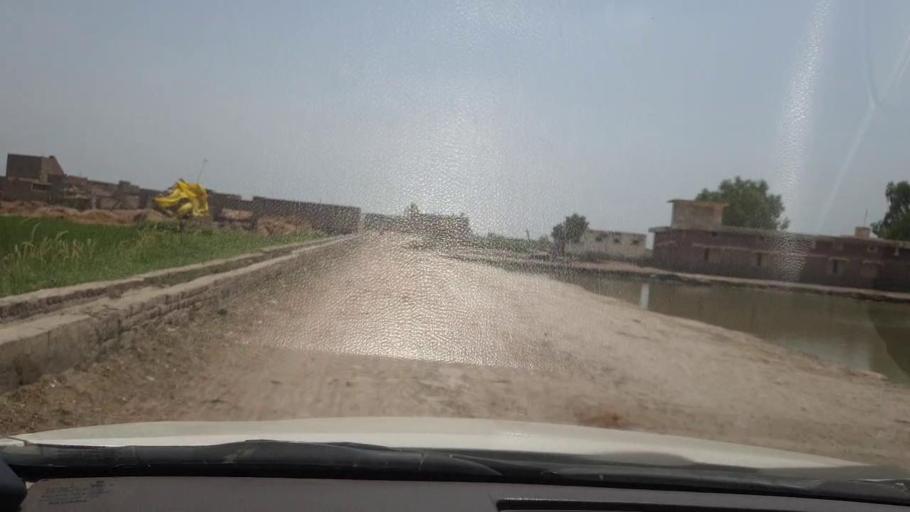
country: PK
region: Sindh
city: Garhi Yasin
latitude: 27.8936
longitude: 68.5566
